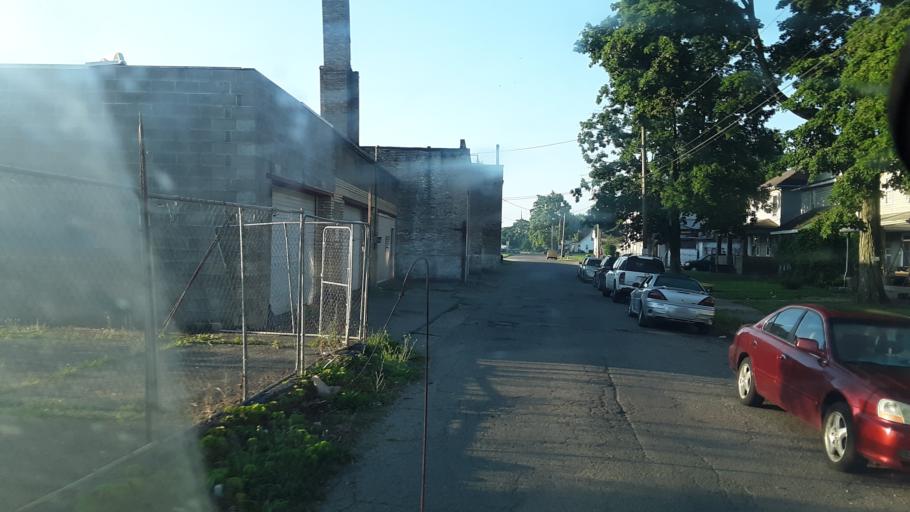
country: US
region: Ohio
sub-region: Licking County
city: Newark
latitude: 40.0661
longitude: -82.4052
